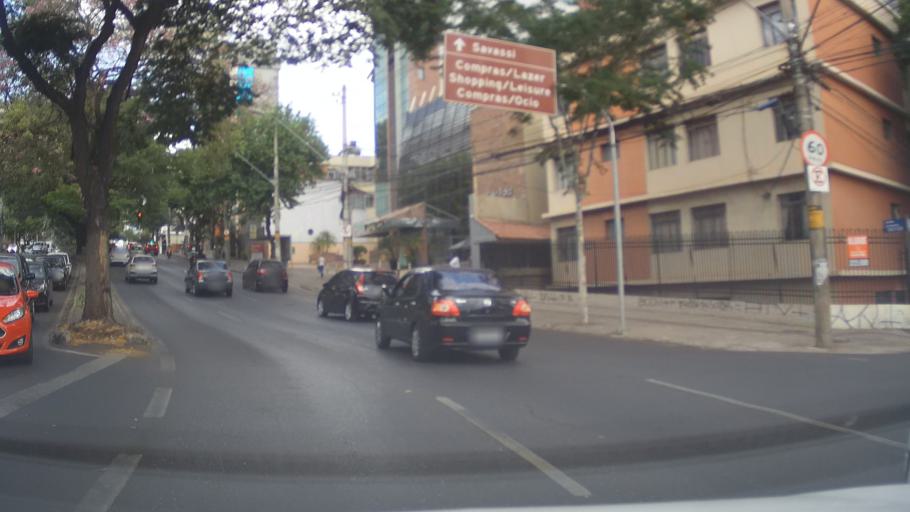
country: BR
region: Minas Gerais
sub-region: Belo Horizonte
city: Belo Horizonte
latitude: -19.9386
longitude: -43.9440
